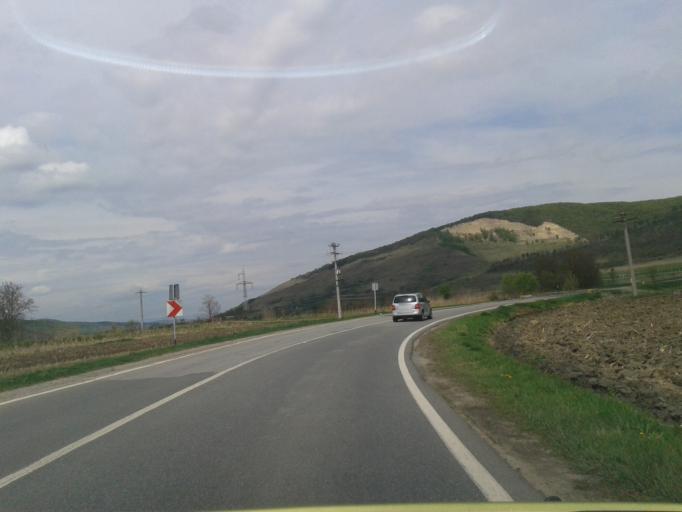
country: RO
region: Sibiu
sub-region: Comuna Micasasa
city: Micasasa
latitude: 46.0773
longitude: 24.0892
